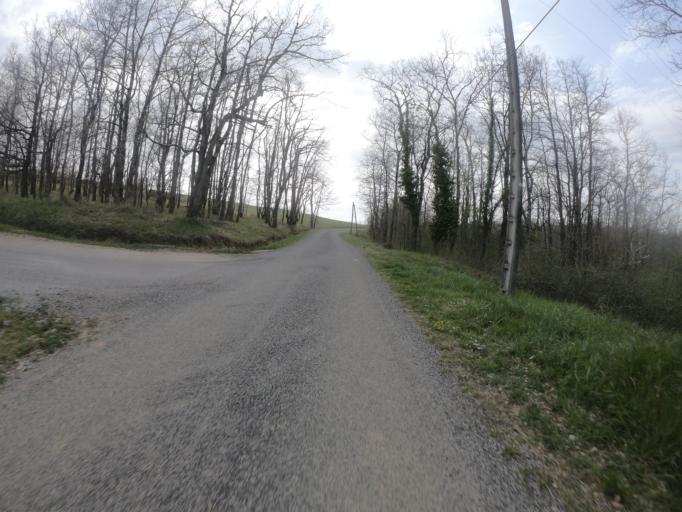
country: FR
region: Languedoc-Roussillon
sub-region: Departement de l'Aude
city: Belpech
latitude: 43.1290
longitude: 1.7465
